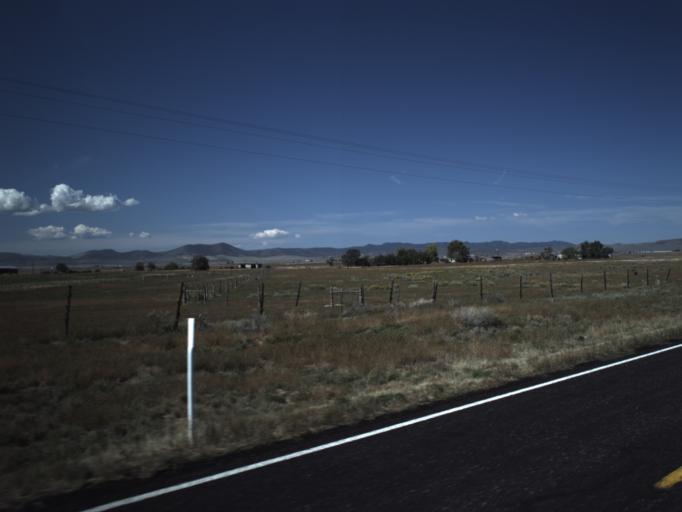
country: US
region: Utah
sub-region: Washington County
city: Enterprise
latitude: 37.6824
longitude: -113.5810
